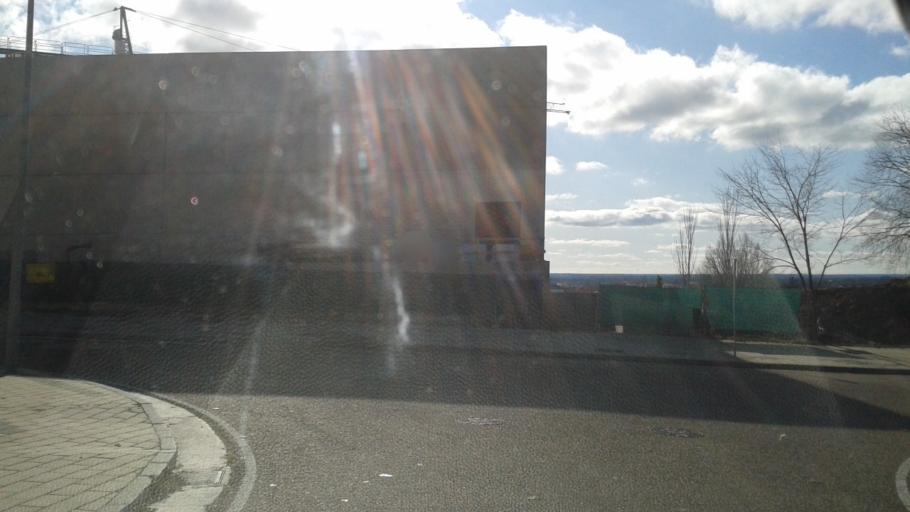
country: ES
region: Castille and Leon
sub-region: Provincia de Valladolid
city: Zaratan
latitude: 41.6328
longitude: -4.7675
